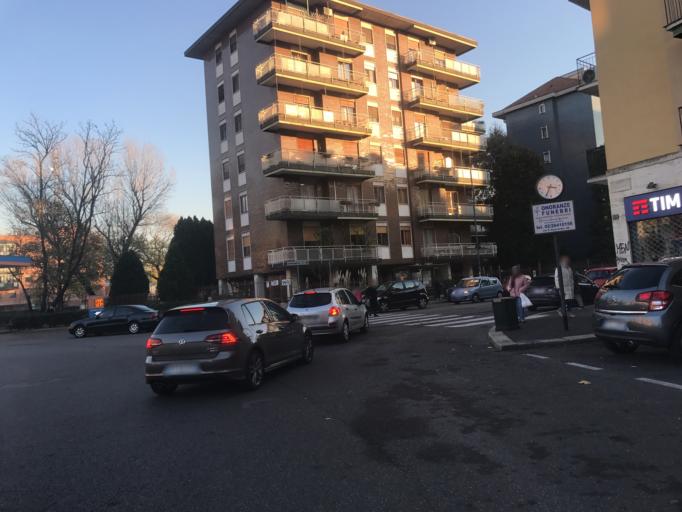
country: IT
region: Lombardy
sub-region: Citta metropolitana di Milano
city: Sesto San Giovanni
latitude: 45.4908
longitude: 9.2368
